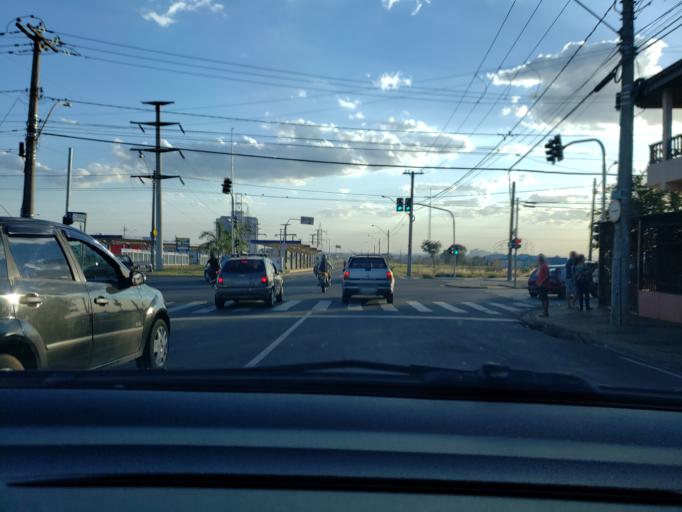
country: BR
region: Sao Paulo
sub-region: Americana
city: Americana
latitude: -22.7349
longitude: -47.3573
